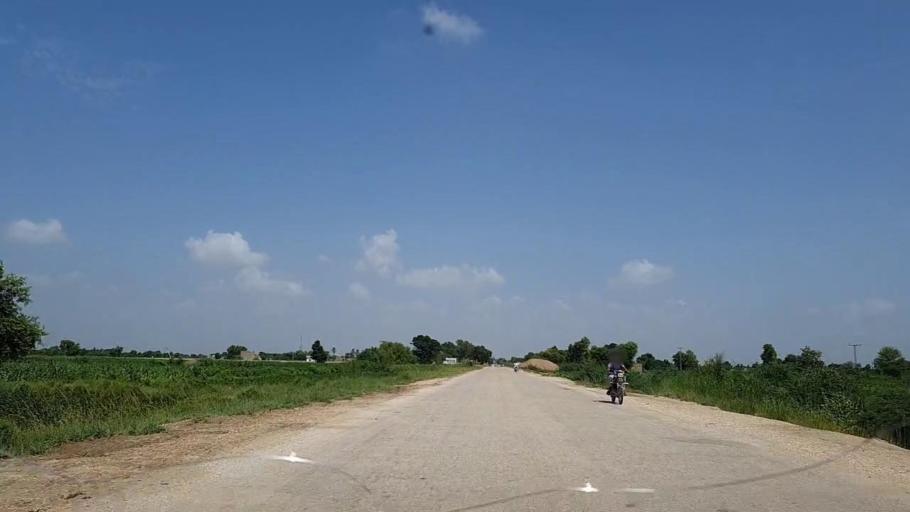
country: PK
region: Sindh
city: Pad Idan
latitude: 26.7866
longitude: 68.2657
